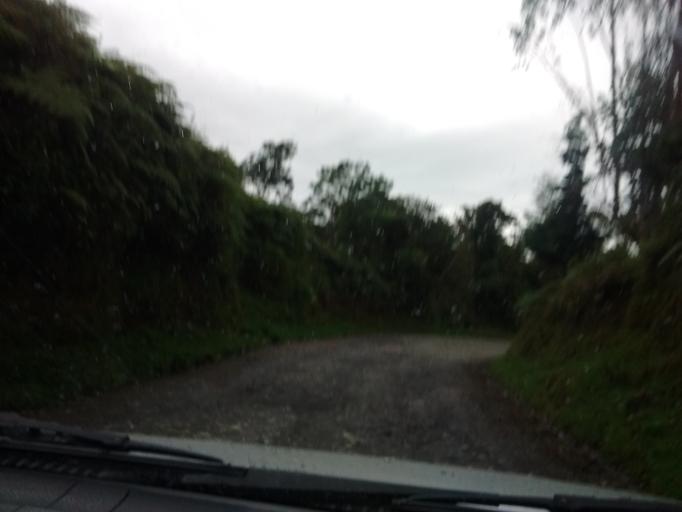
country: CO
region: Huila
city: La Argentina
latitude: 2.2626
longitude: -76.1972
